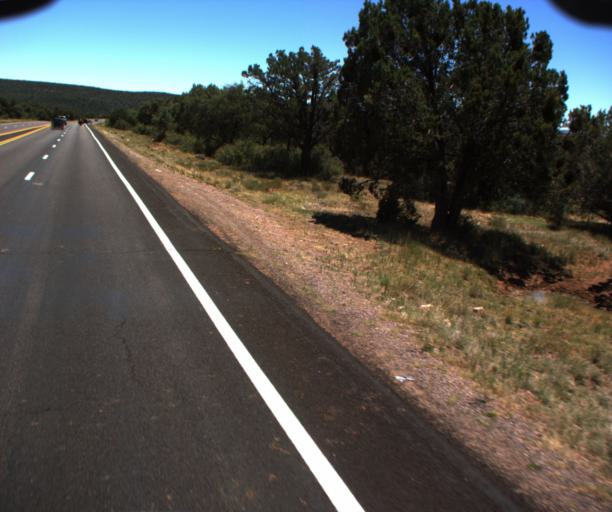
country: US
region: Arizona
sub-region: Gila County
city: Pine
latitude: 34.3318
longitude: -111.4195
